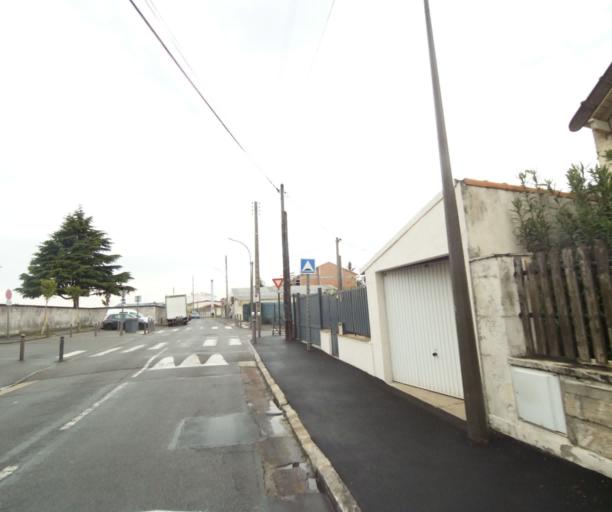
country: FR
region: Ile-de-France
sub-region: Departement du Val-d'Oise
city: Bezons
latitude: 48.9392
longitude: 2.2121
